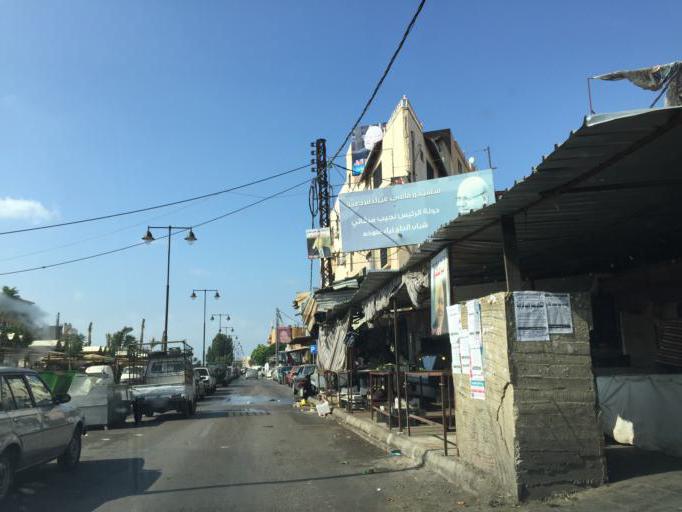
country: LB
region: Liban-Nord
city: Tripoli
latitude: 34.4385
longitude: 35.8473
